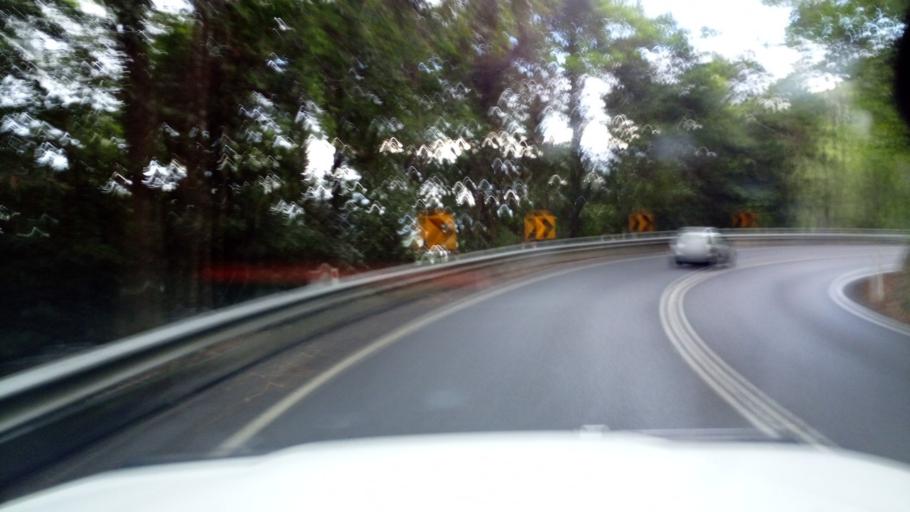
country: AU
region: Queensland
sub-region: Cairns
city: Redlynch
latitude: -16.8467
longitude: 145.6757
